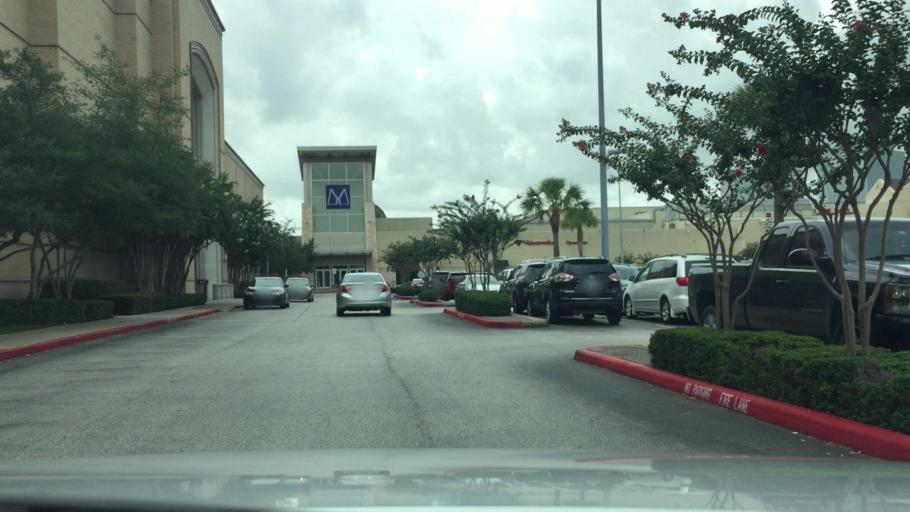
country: US
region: Texas
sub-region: Harris County
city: Bunker Hill Village
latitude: 29.7827
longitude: -95.5401
